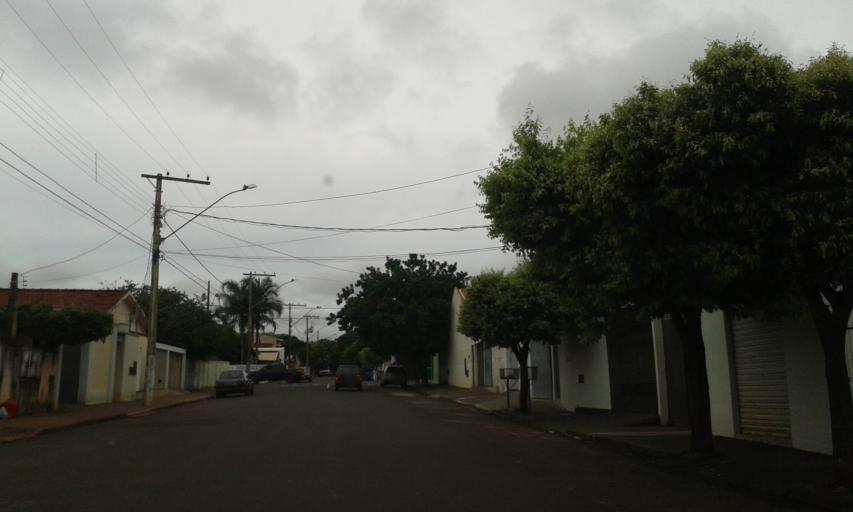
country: BR
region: Minas Gerais
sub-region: Ituiutaba
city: Ituiutaba
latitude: -18.9806
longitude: -49.4540
